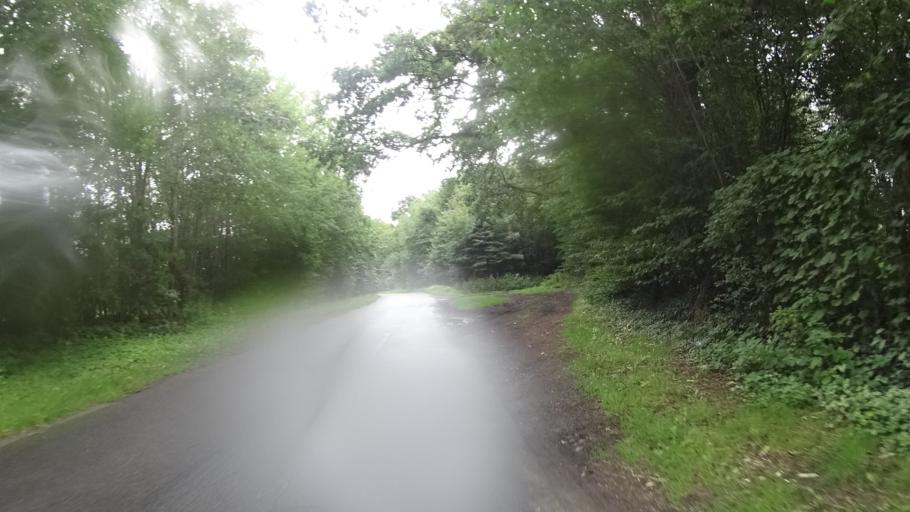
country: DE
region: Schleswig-Holstein
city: Bilsen
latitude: 53.7750
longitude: 9.8849
